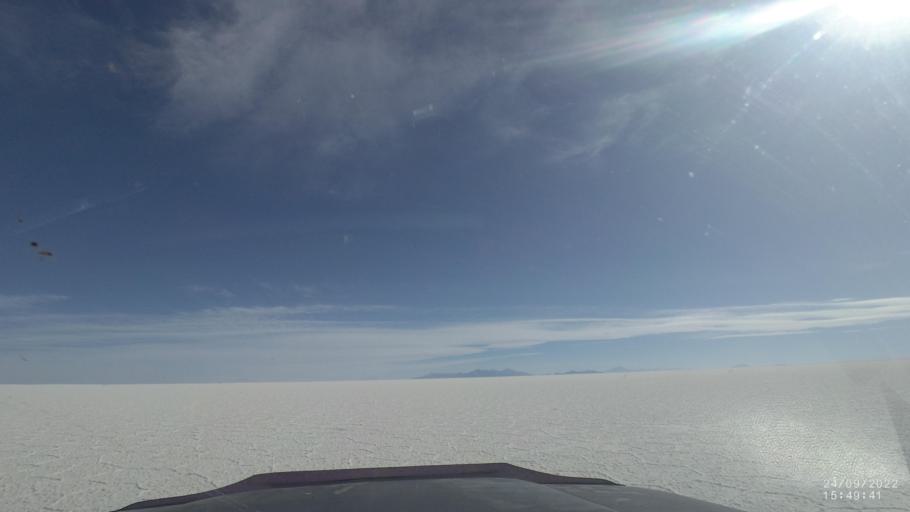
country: BO
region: Potosi
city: Colchani
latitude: -20.3026
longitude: -67.2433
